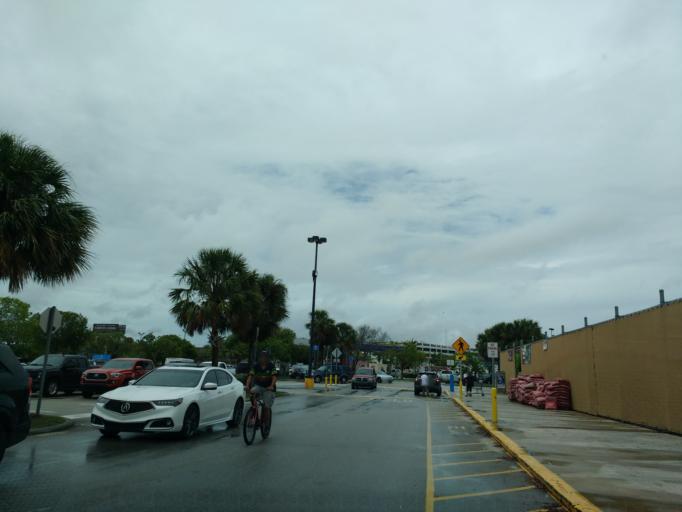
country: US
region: Florida
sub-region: Miami-Dade County
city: Florida City
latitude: 25.4568
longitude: -80.4732
